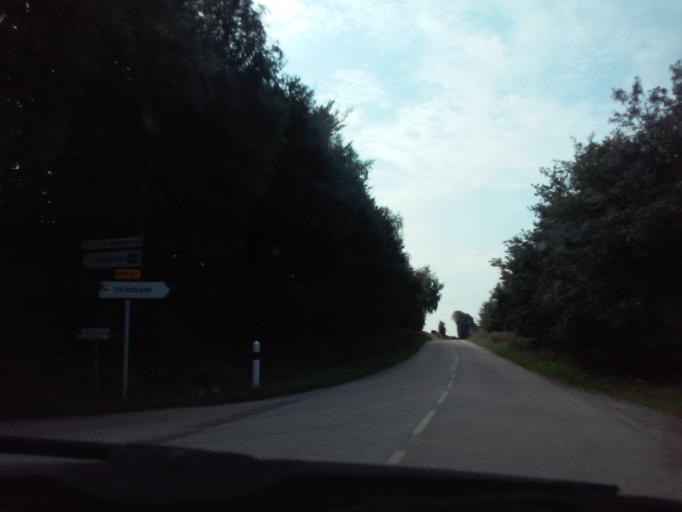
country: FR
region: Brittany
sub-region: Departement du Morbihan
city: Ploermel
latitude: 47.9072
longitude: -2.4100
